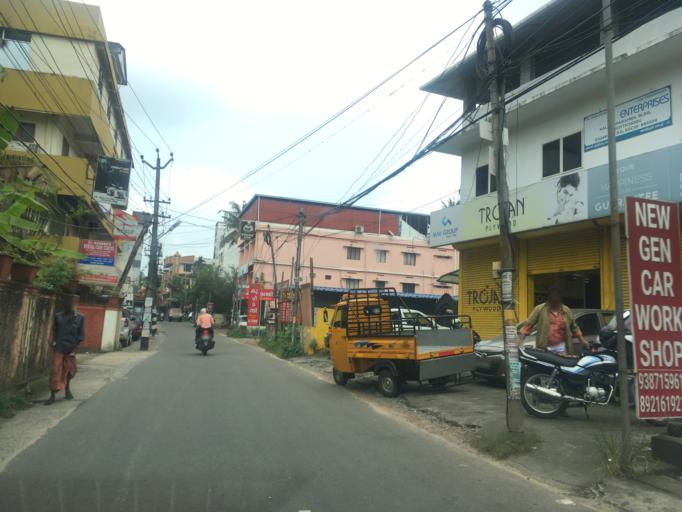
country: IN
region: Kerala
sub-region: Ernakulam
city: Elur
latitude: 10.0246
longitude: 76.3127
